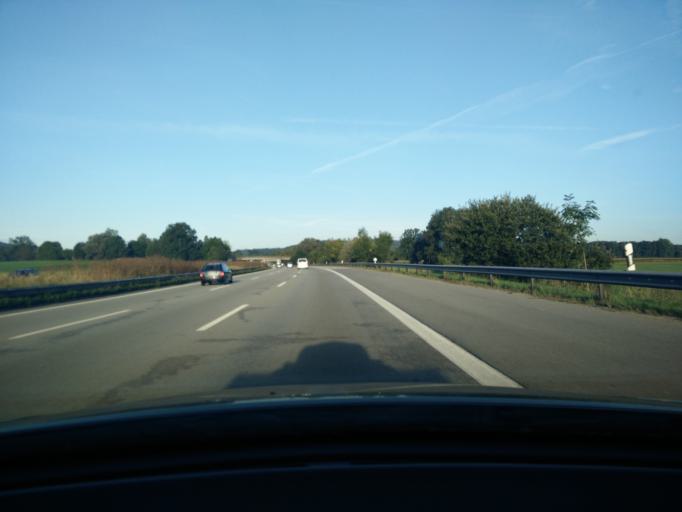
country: DE
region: Bavaria
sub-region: Upper Bavaria
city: Bad Aibling
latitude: 47.8220
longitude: 11.9916
